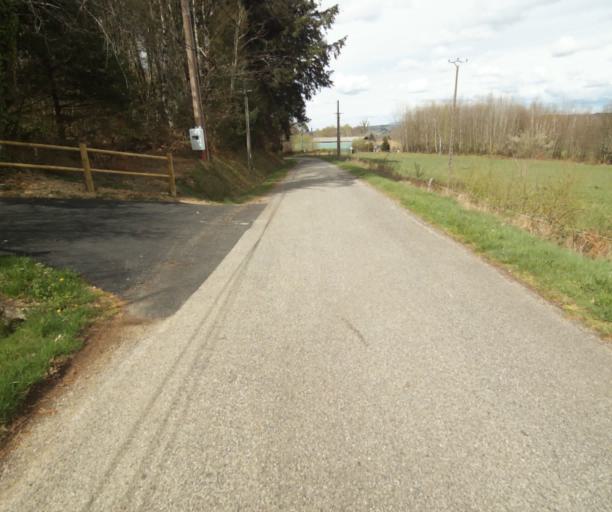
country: FR
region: Limousin
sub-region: Departement de la Correze
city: Laguenne
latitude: 45.2301
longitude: 1.8726
